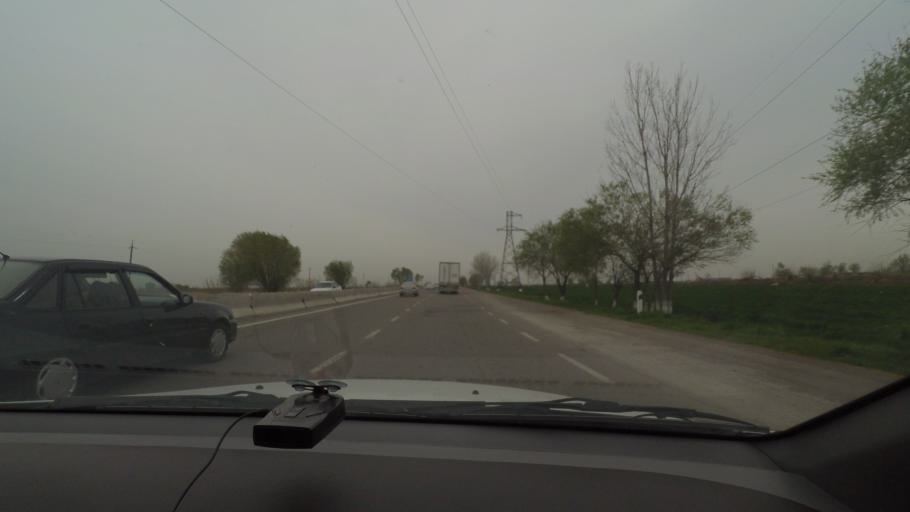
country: KZ
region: Ongtustik Qazaqstan
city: Myrzakent
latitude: 40.5242
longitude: 68.4528
